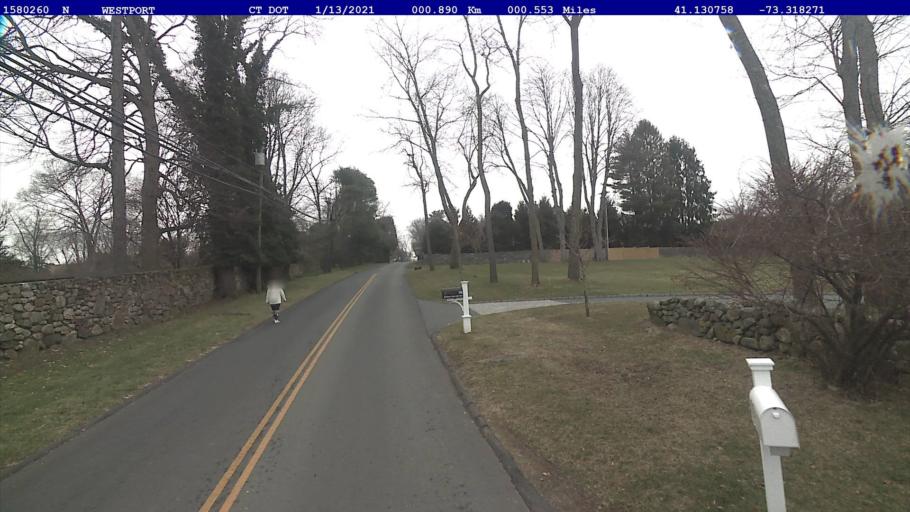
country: US
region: Connecticut
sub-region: Fairfield County
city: Southport
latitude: 41.1308
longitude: -73.3183
